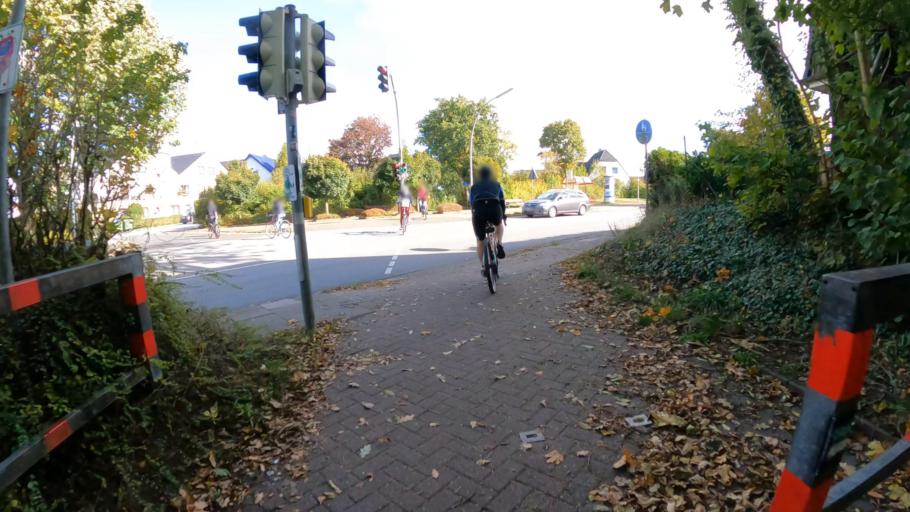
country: DE
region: Schleswig-Holstein
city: Henstedt-Ulzburg
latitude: 53.7921
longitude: 9.9980
